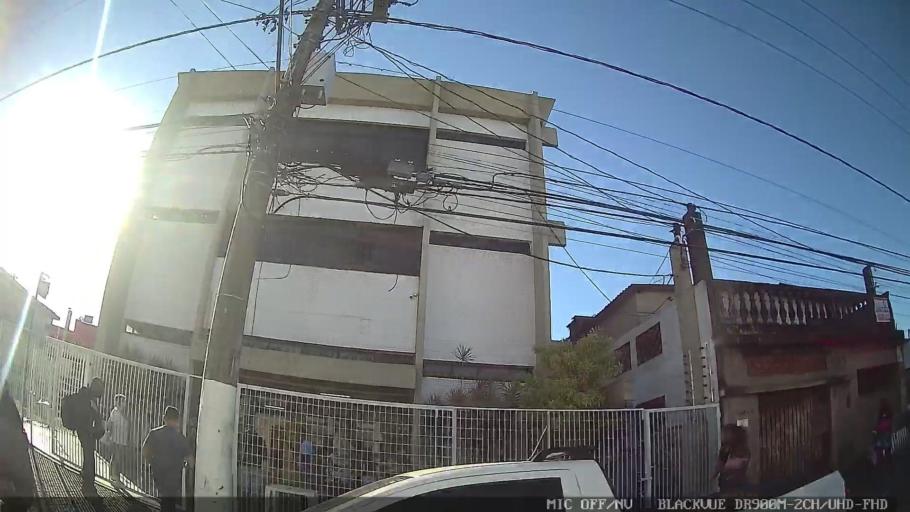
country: BR
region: Sao Paulo
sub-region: Santos
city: Santos
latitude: -23.9571
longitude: -46.2924
